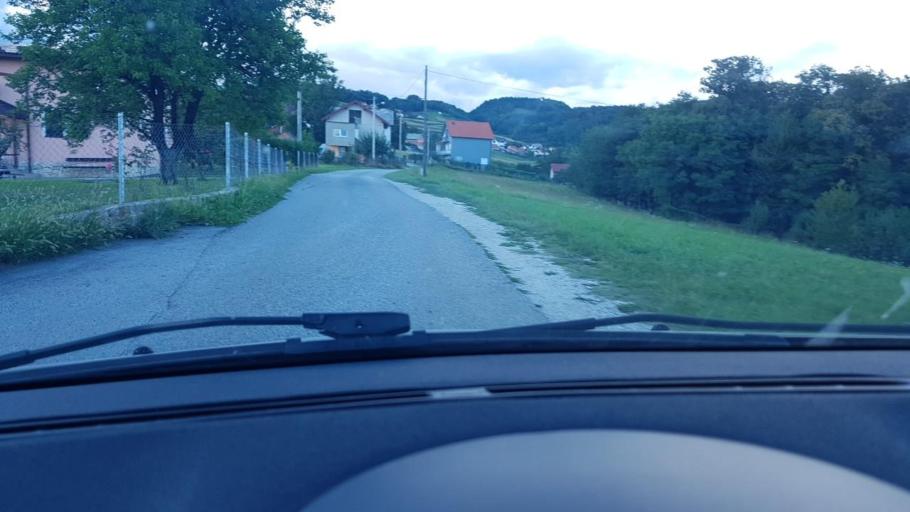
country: HR
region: Krapinsko-Zagorska
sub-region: Grad Krapina
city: Krapina
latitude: 46.1660
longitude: 15.8279
